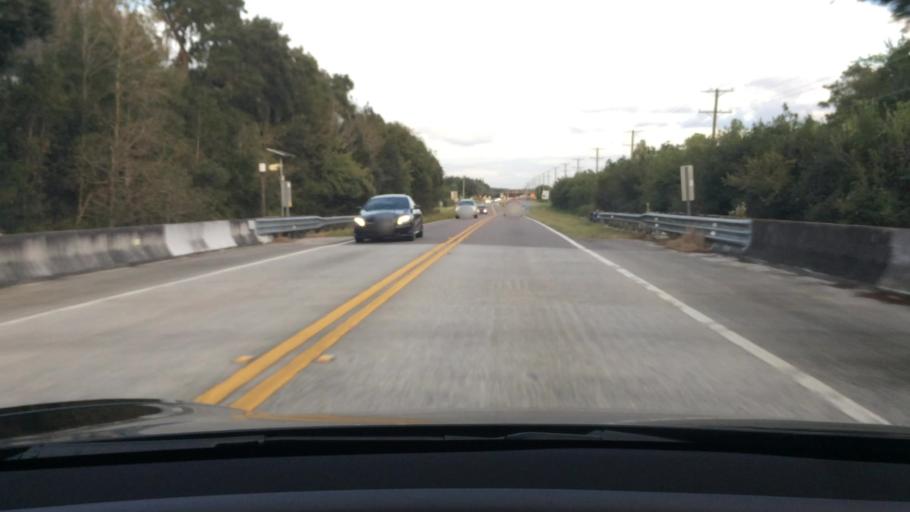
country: US
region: Florida
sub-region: Hillsborough County
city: Pebble Creek
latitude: 28.1712
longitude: -82.3618
